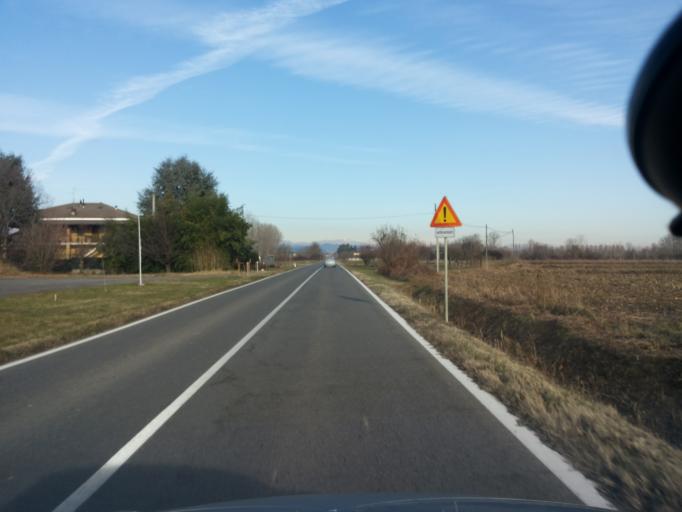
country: IT
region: Piedmont
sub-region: Provincia di Vercelli
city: Ghislarengo
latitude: 45.5146
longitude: 8.3874
